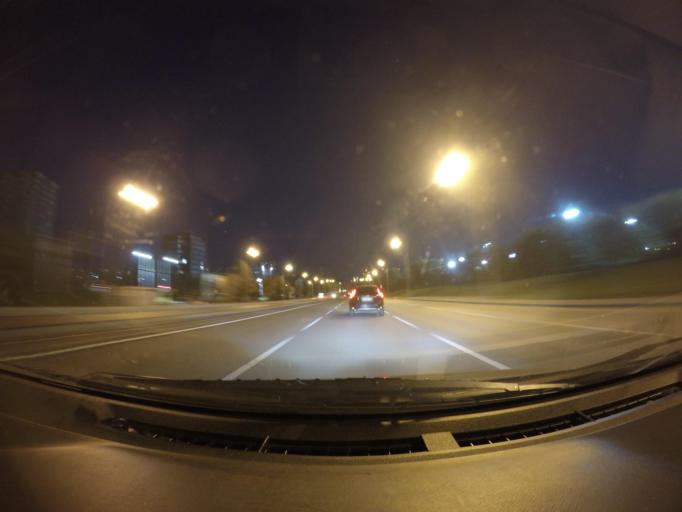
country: RU
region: Moskovskaya
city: Bogorodskoye
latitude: 55.8080
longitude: 37.6986
